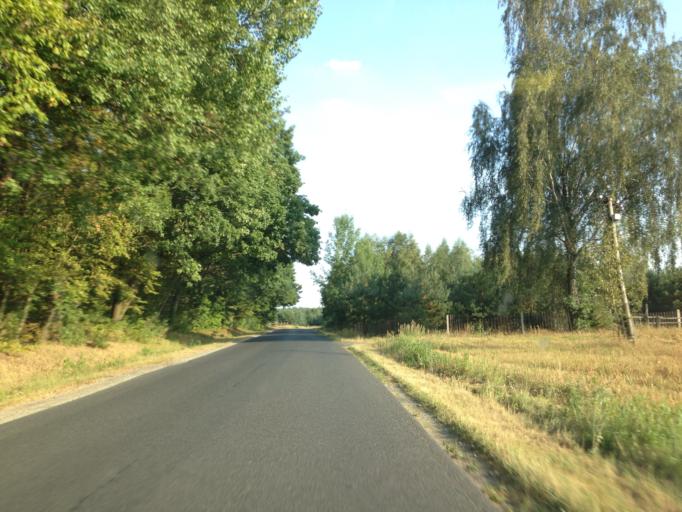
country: PL
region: Warmian-Masurian Voivodeship
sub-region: Powiat nowomiejski
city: Biskupiec
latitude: 53.3884
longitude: 19.3749
